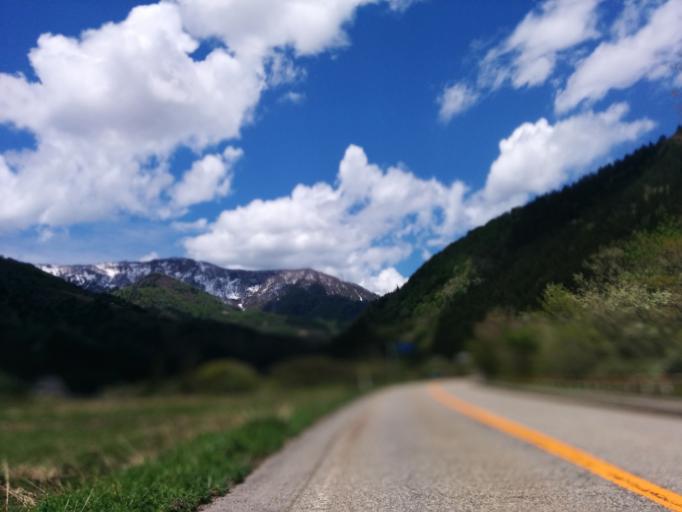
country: JP
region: Toyama
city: Fukumitsu
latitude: 36.3647
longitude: 136.8730
